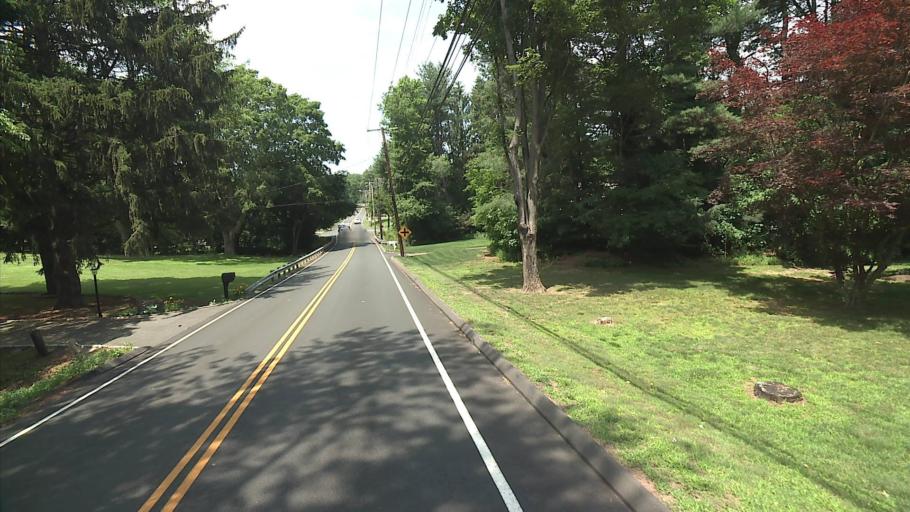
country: US
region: Connecticut
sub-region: New Haven County
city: Hamden
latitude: 41.3933
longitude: -72.8788
